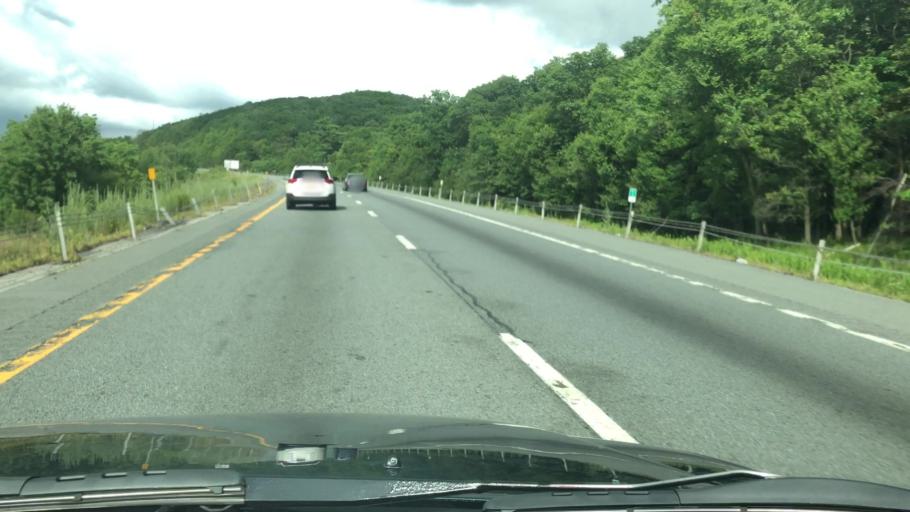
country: US
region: New York
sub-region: Orange County
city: Port Jervis
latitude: 41.3652
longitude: -74.6521
